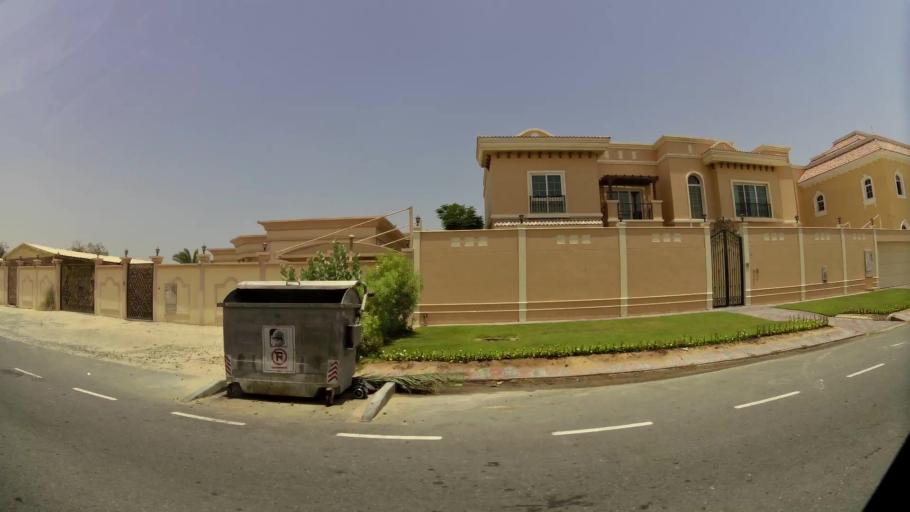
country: AE
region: Dubai
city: Dubai
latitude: 25.0941
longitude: 55.2370
